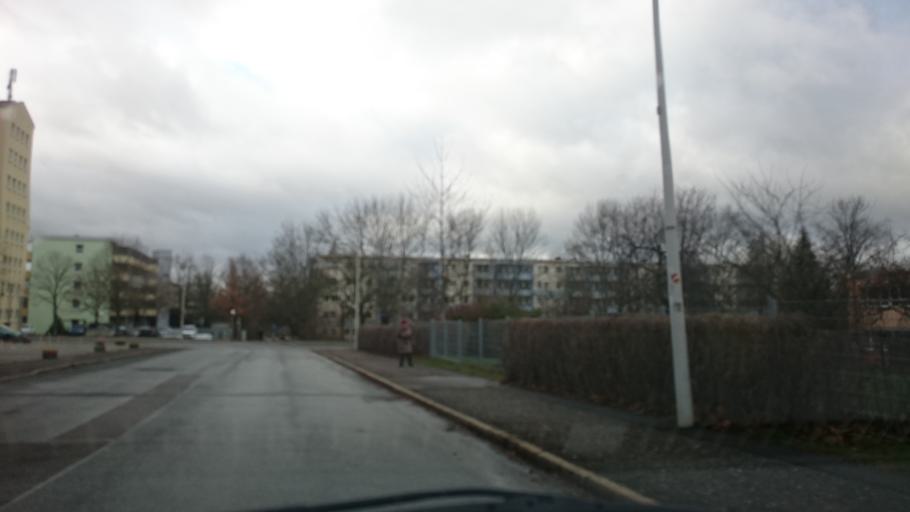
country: DE
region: Saxony
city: Zwickau
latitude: 50.7359
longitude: 12.5124
